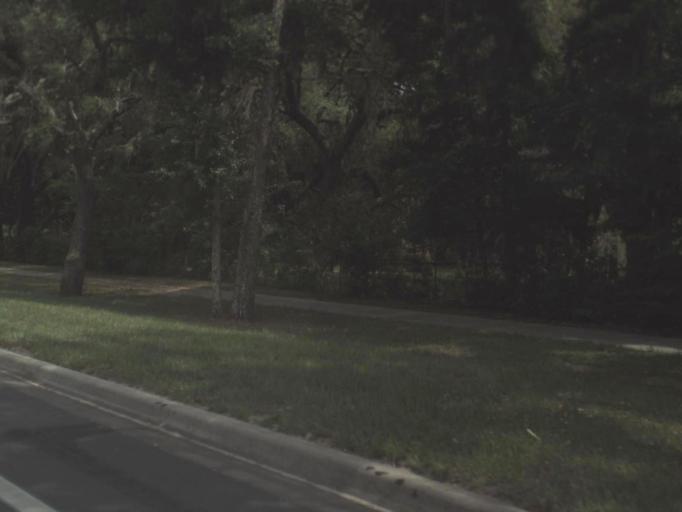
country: US
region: Florida
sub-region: Putnam County
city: Interlachen
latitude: 29.6293
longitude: -81.8747
